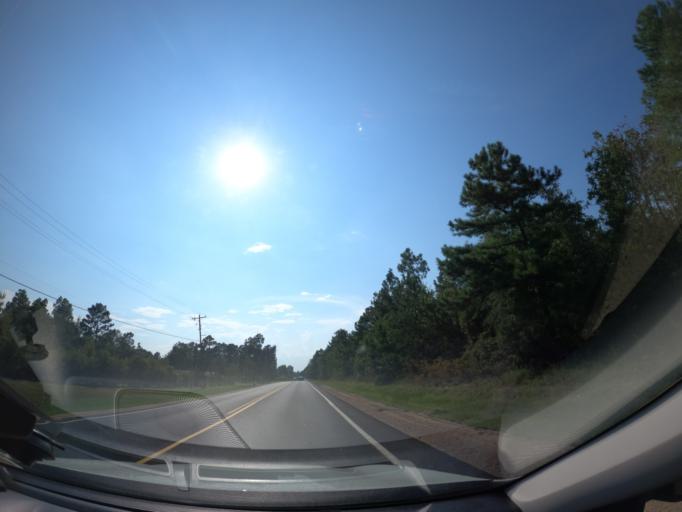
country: US
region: South Carolina
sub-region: Aiken County
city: New Ellenton
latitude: 33.3932
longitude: -81.7305
